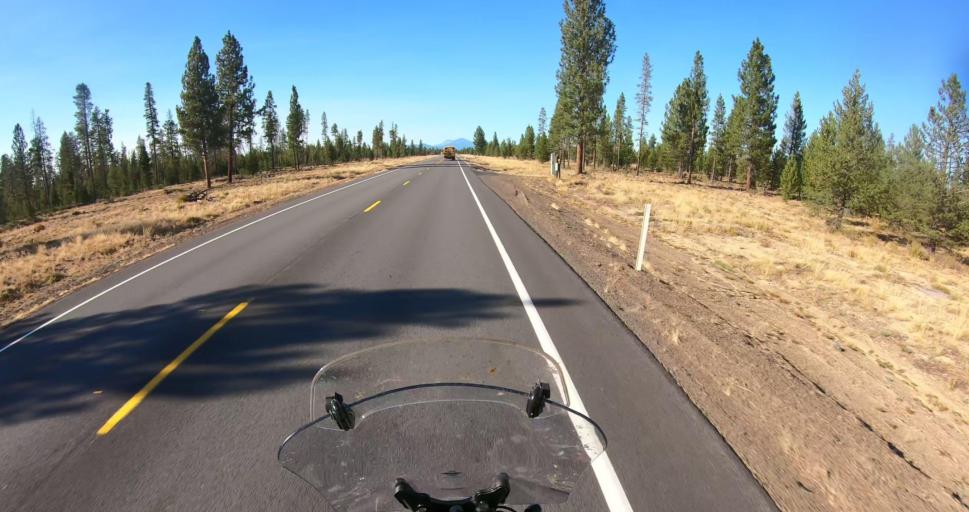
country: US
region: Oregon
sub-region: Deschutes County
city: La Pine
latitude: 43.6006
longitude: -121.4978
